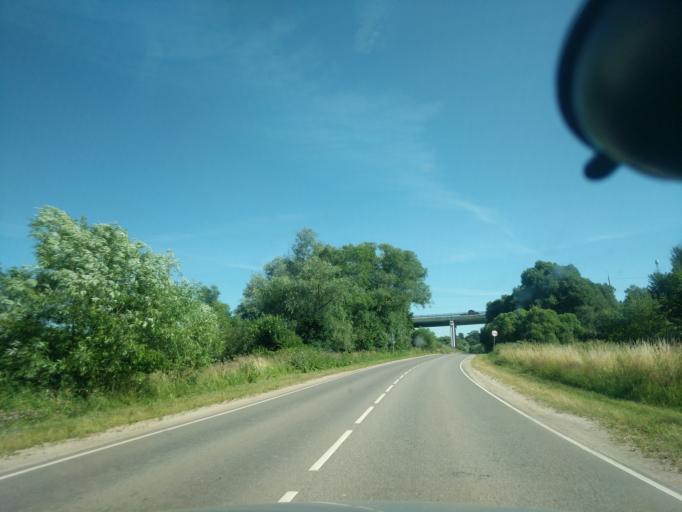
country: RU
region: Moskovskaya
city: Serpukhov
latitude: 54.8588
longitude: 37.4788
